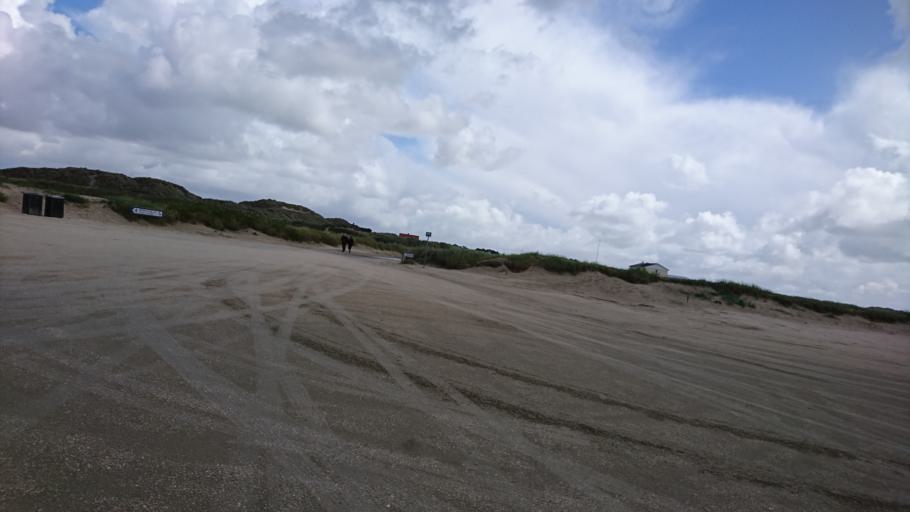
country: DK
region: South Denmark
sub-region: Fano Kommune
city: Nordby
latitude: 55.3467
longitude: 8.4381
